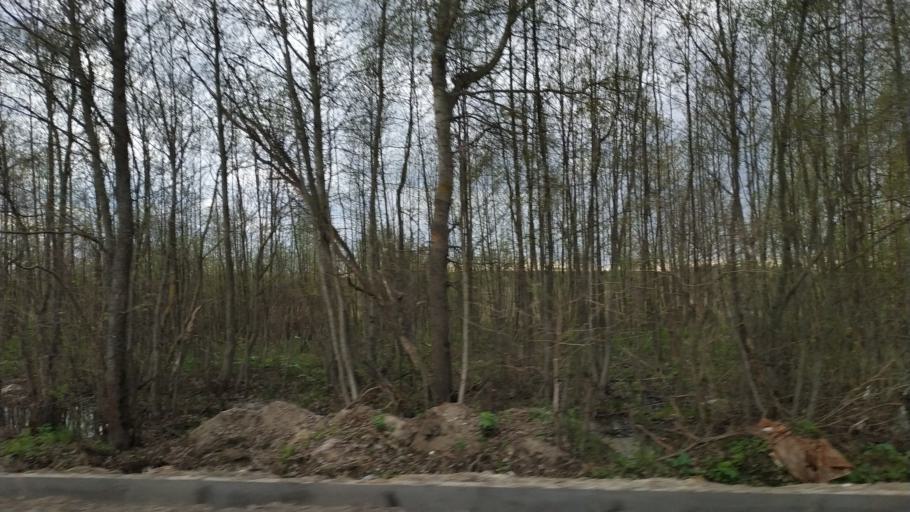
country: RU
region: Moskovskaya
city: Pavlovskiy Posad
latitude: 55.7988
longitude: 38.6870
